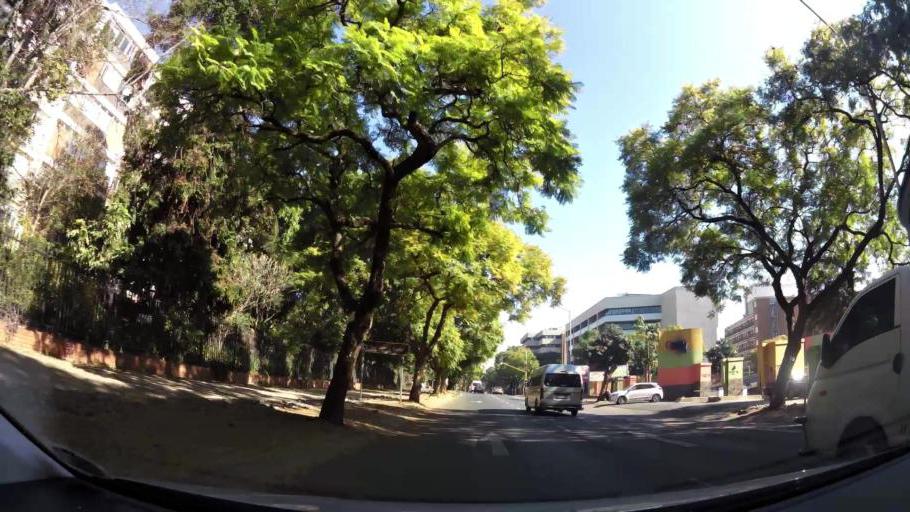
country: ZA
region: Gauteng
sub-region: City of Tshwane Metropolitan Municipality
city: Pretoria
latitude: -25.7587
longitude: 28.2043
